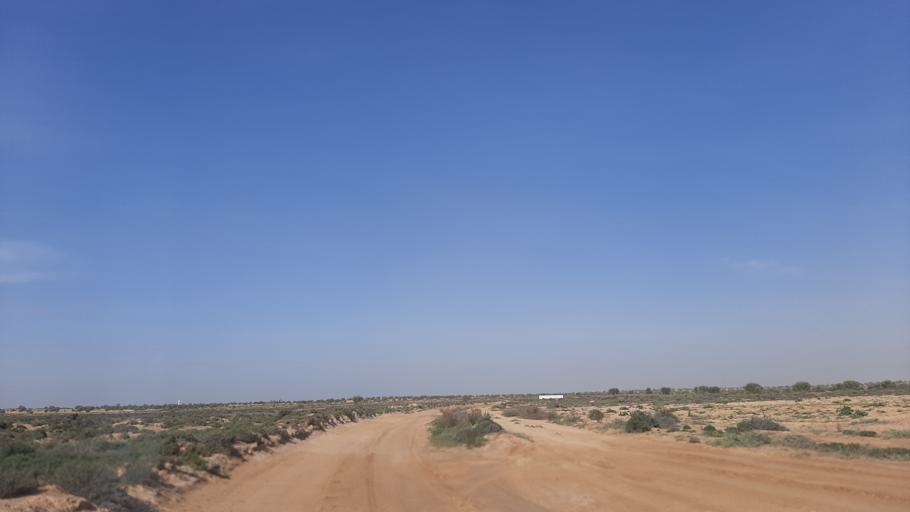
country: TN
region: Madanin
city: Zarzis
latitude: 33.4473
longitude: 10.8078
